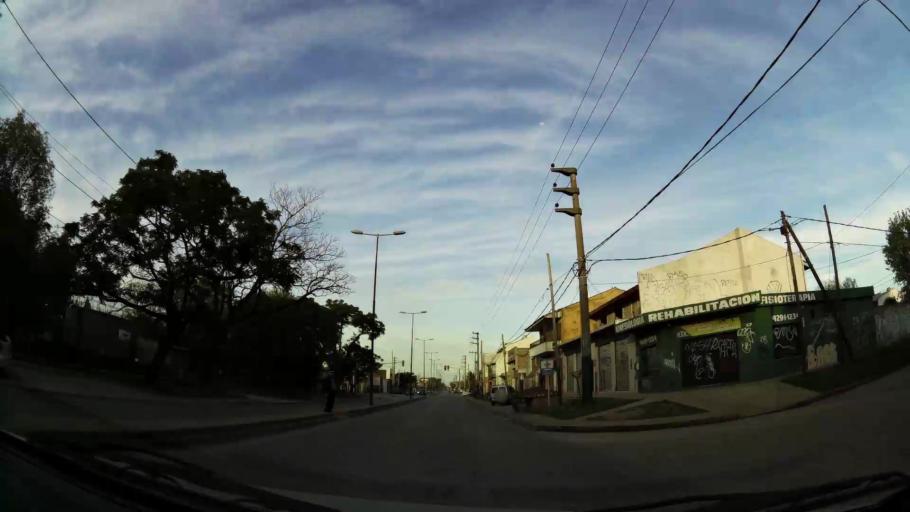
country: AR
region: Buenos Aires
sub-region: Partido de Almirante Brown
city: Adrogue
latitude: -34.7875
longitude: -58.3495
